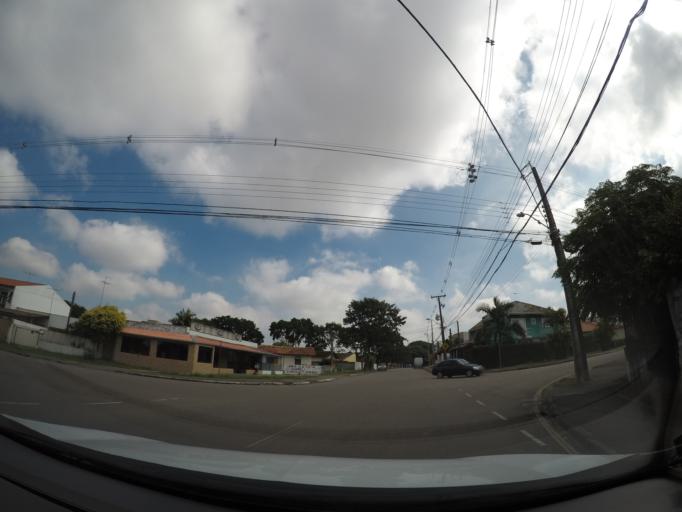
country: BR
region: Parana
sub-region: Sao Jose Dos Pinhais
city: Sao Jose dos Pinhais
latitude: -25.4931
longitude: -49.2228
